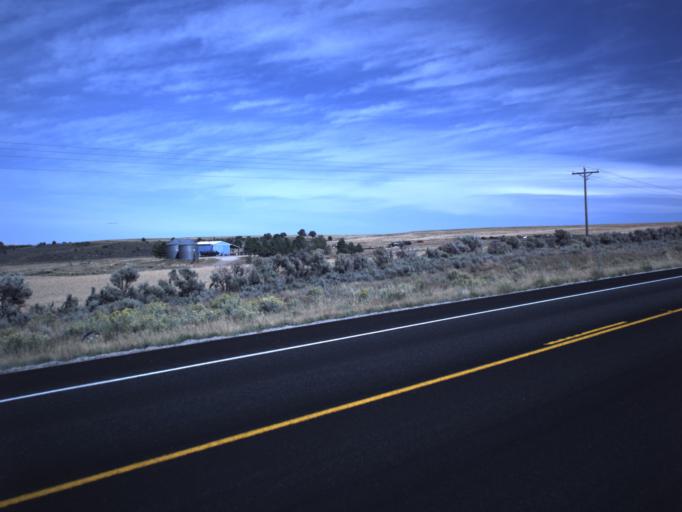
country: US
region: Utah
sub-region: San Juan County
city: Monticello
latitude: 37.8728
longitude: -109.2663
